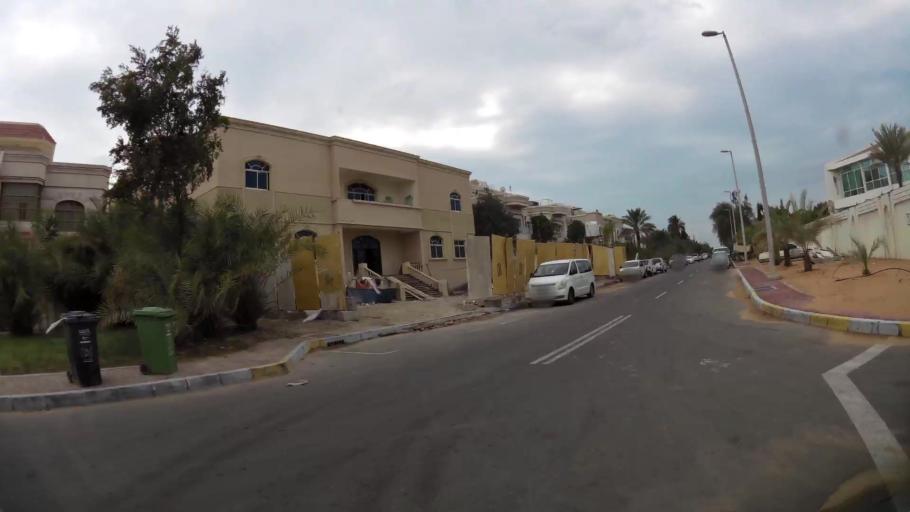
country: AE
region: Abu Dhabi
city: Abu Dhabi
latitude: 24.4289
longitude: 54.3996
